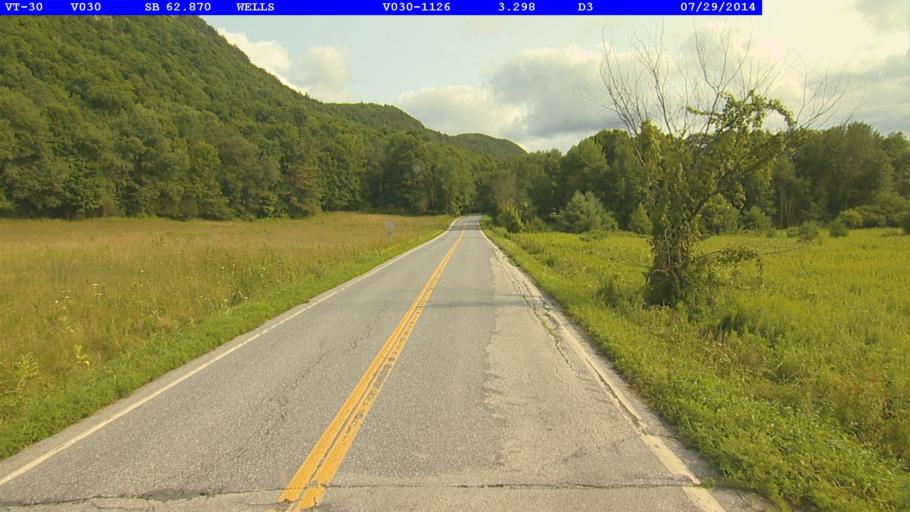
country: US
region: New York
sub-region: Washington County
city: Granville
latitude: 43.4414
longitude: -73.1953
